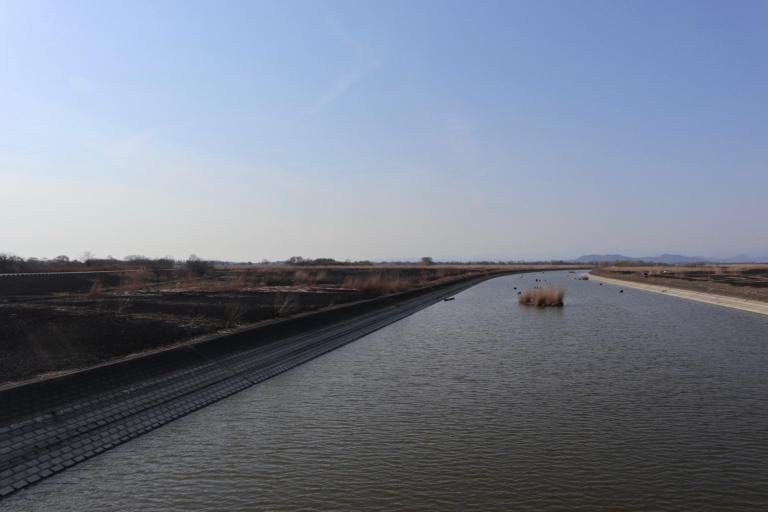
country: JP
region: Tochigi
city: Fujioka
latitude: 36.2250
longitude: 139.6854
